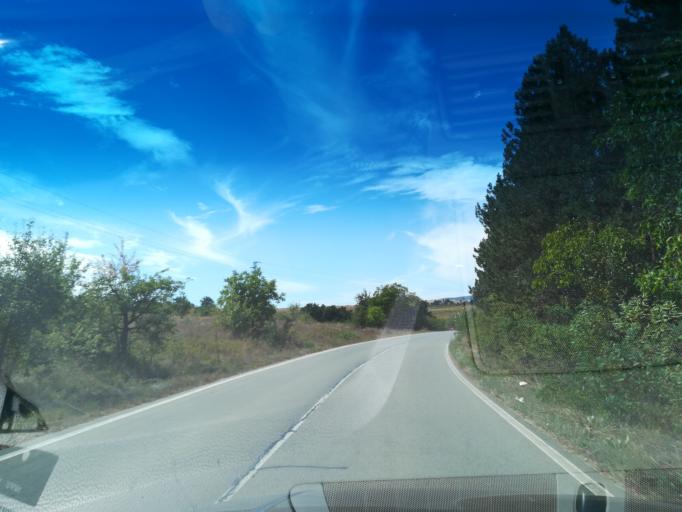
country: BG
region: Plovdiv
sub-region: Obshtina Suedinenie
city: Suedinenie
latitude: 42.3997
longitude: 24.5401
